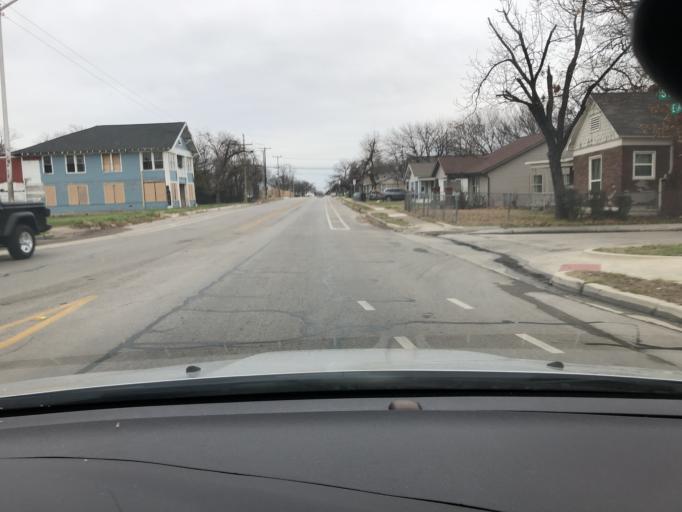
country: US
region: Texas
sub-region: Tarrant County
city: Fort Worth
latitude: 32.7261
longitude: -97.3173
